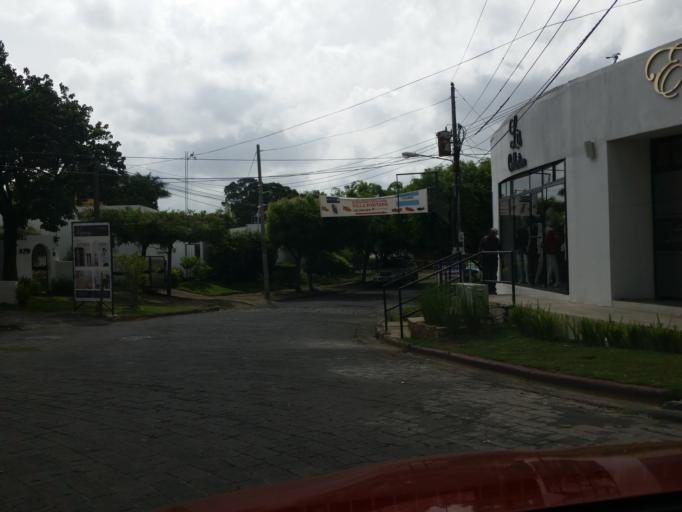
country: NI
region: Managua
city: Managua
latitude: 12.1039
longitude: -86.2653
